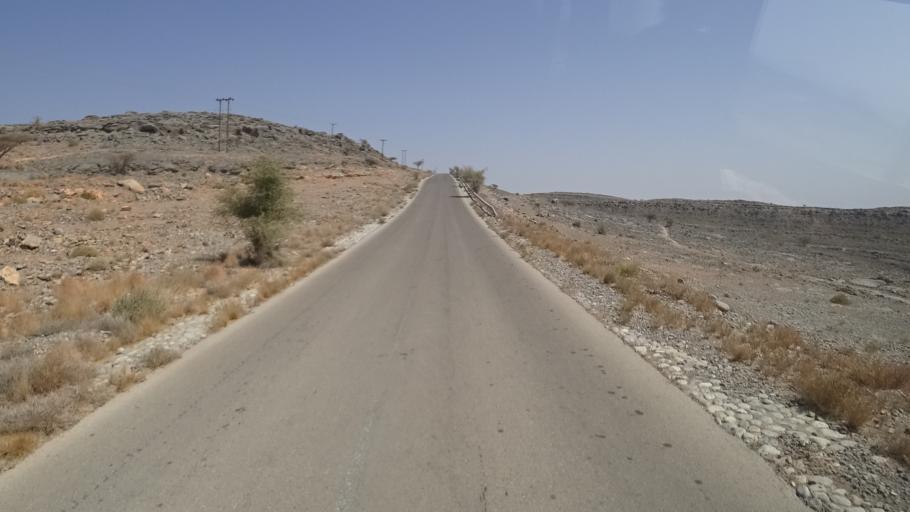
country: OM
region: Muhafazat ad Dakhiliyah
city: Bahla'
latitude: 23.0978
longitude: 57.3846
